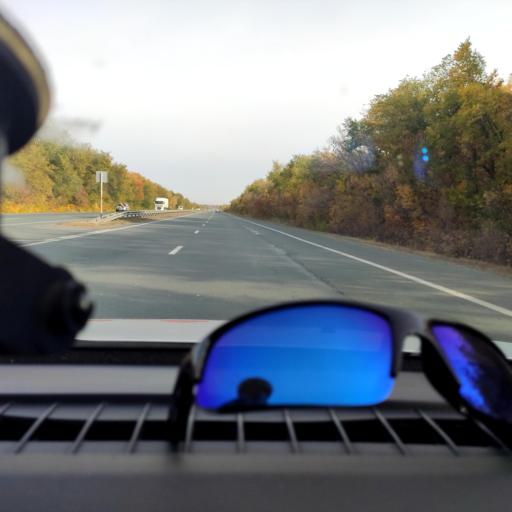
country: RU
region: Samara
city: Novokuybyshevsk
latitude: 53.0298
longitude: 49.9943
